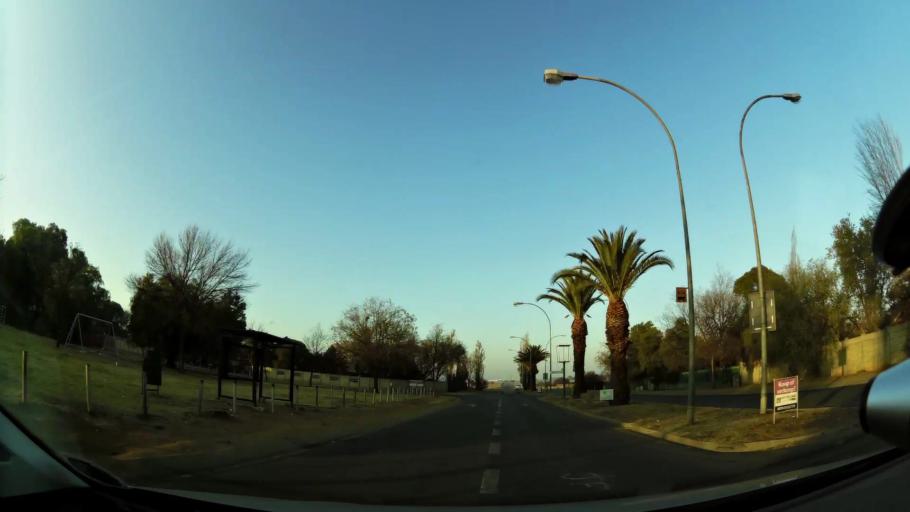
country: ZA
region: Orange Free State
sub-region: Mangaung Metropolitan Municipality
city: Bloemfontein
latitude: -29.1074
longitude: 26.1556
